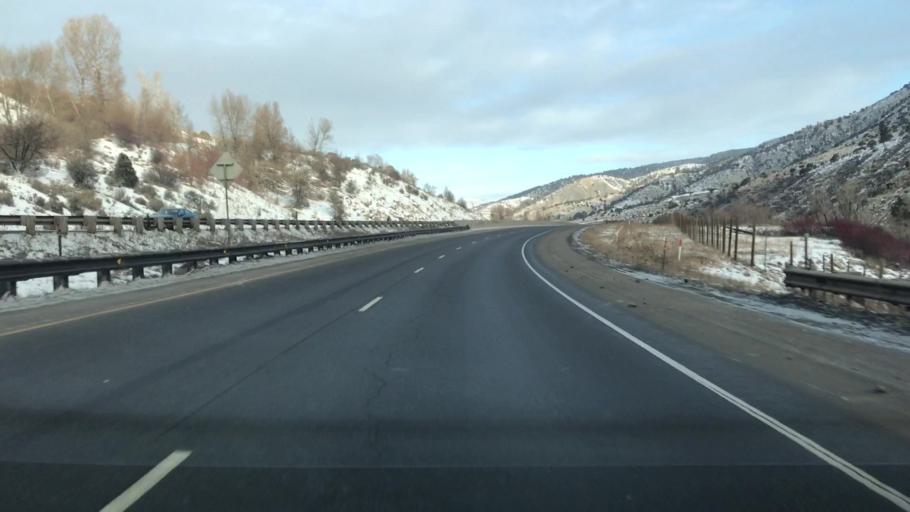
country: US
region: Colorado
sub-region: Eagle County
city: Edwards
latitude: 39.6757
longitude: -106.6476
